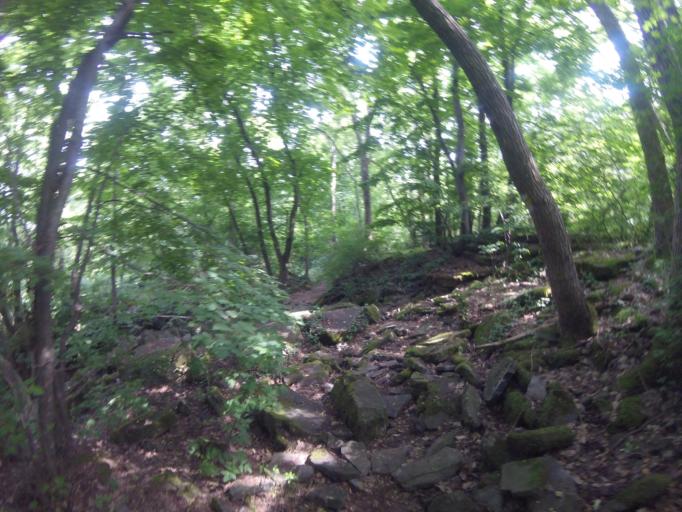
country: HU
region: Zala
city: Turje
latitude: 46.9116
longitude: 17.1743
